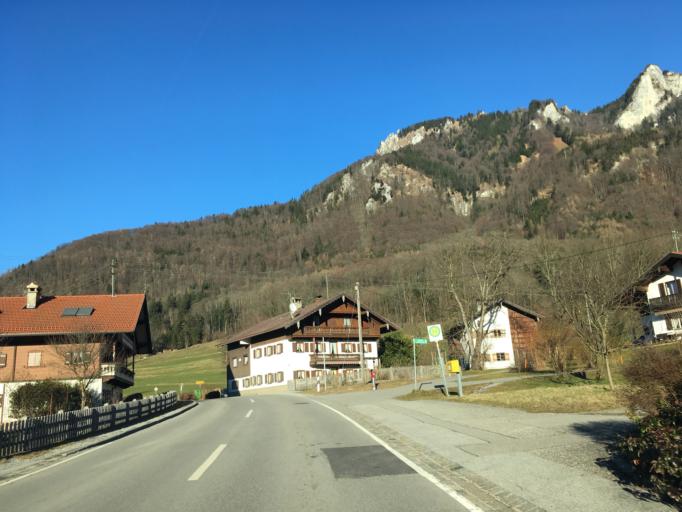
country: DE
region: Bavaria
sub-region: Upper Bavaria
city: Nussdorf am Inn
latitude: 47.7170
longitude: 12.1647
